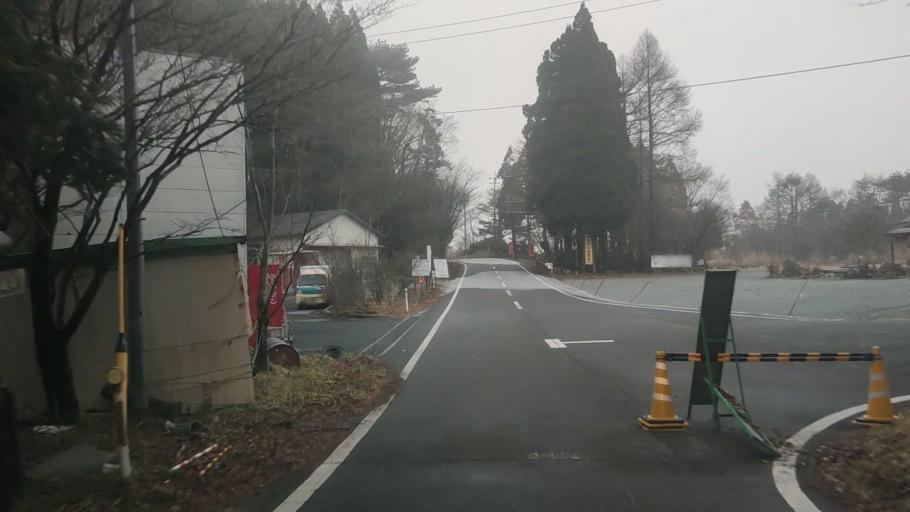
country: JP
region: Kumamoto
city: Matsubase
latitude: 32.5747
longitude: 130.9026
